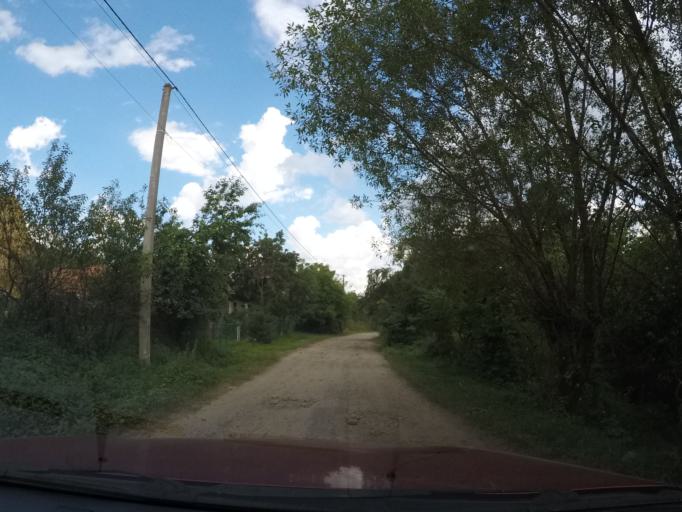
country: UA
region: Zakarpattia
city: Velykyi Bereznyi
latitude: 49.0320
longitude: 22.5840
